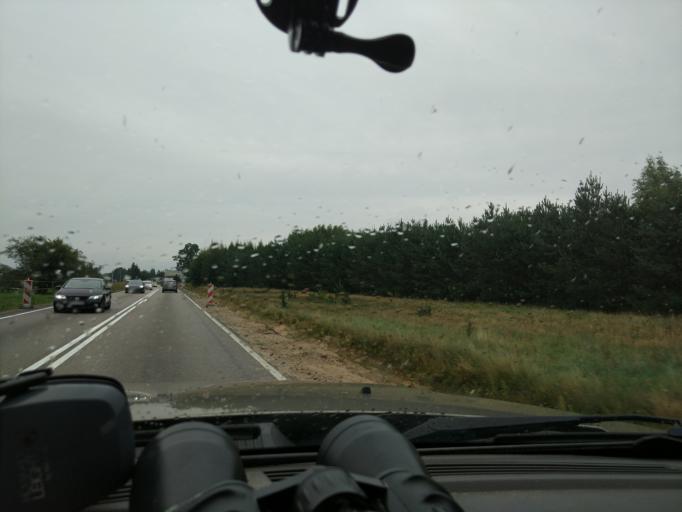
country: PL
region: Masovian Voivodeship
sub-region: Powiat ostrowski
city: Brok
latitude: 52.7558
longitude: 21.7939
